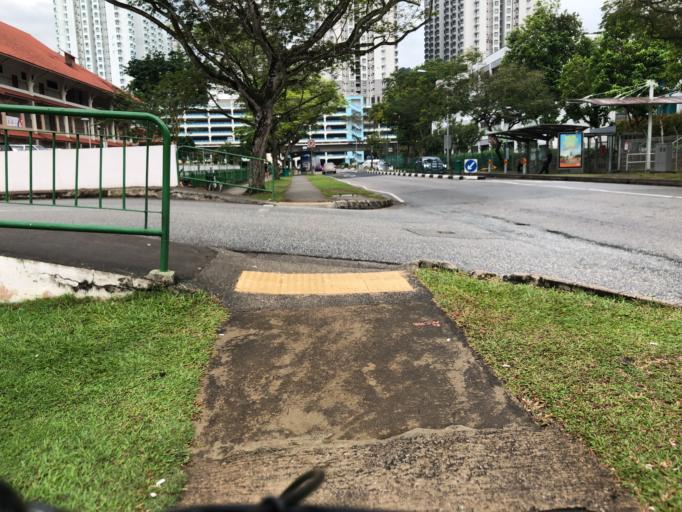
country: MY
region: Johor
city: Johor Bahru
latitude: 1.3654
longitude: 103.7500
